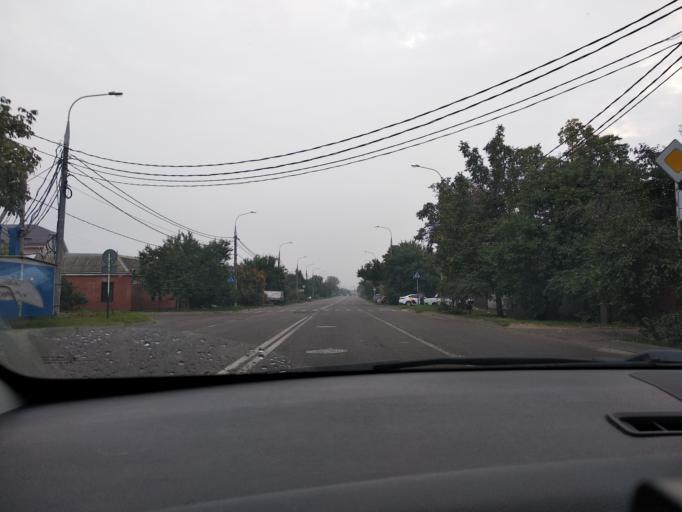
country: RU
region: Krasnodarskiy
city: Krasnodar
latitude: 45.0151
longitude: 38.9995
